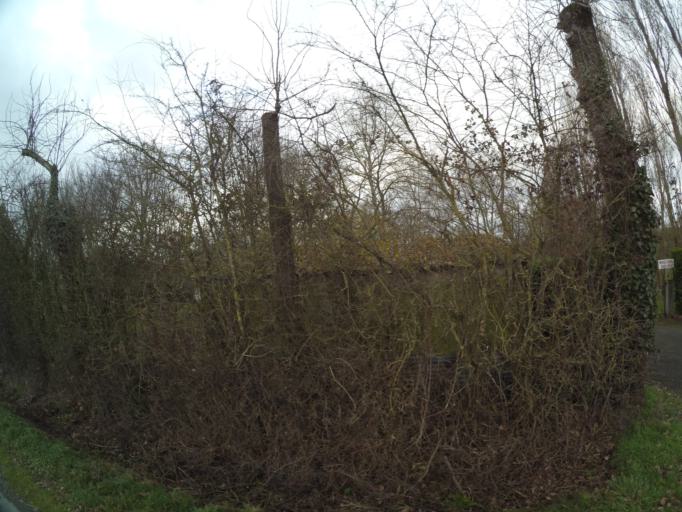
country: FR
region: Pays de la Loire
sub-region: Departement de la Vendee
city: Saint-Hilaire-de-Loulay
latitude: 47.0065
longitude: -1.3213
